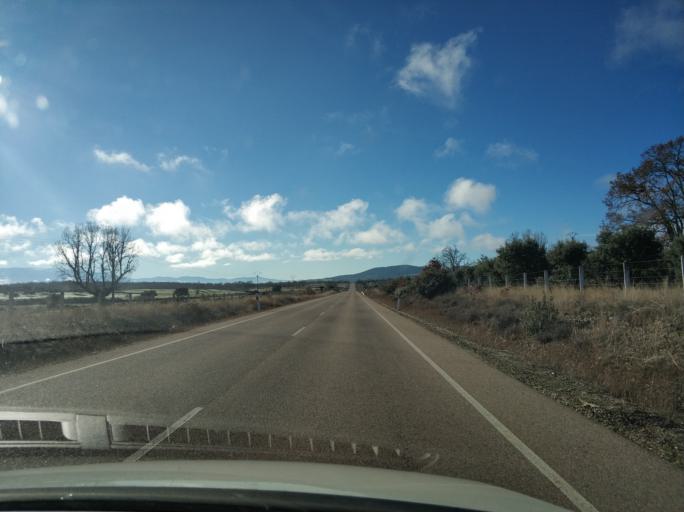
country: ES
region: Castille and Leon
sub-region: Provincia de Salamanca
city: Herguijuela del Campo
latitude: 40.6441
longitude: -5.9022
